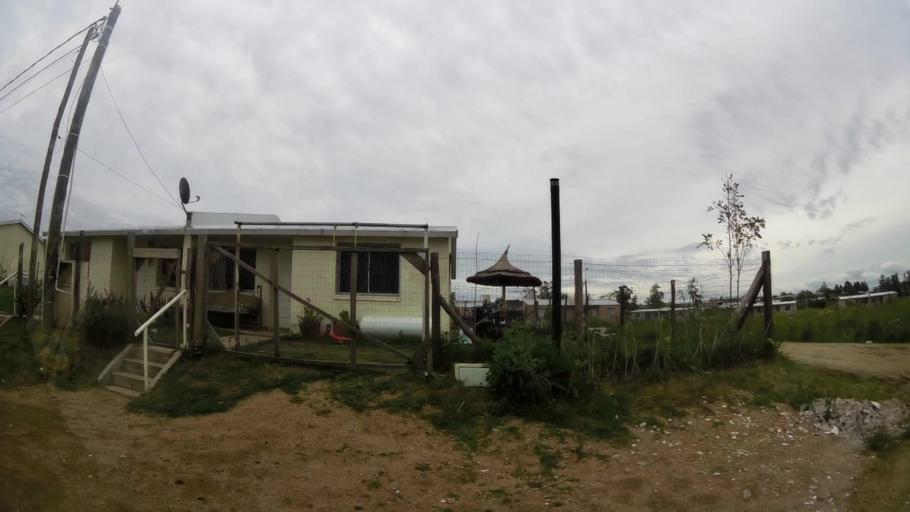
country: UY
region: Maldonado
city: Maldonado
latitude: -34.8874
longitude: -54.9483
